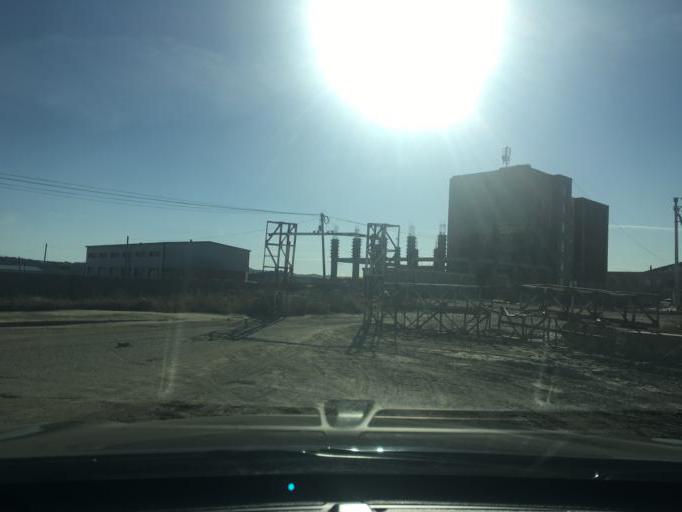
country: MN
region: Ulaanbaatar
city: Ulaanbaatar
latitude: 47.8875
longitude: 106.7727
